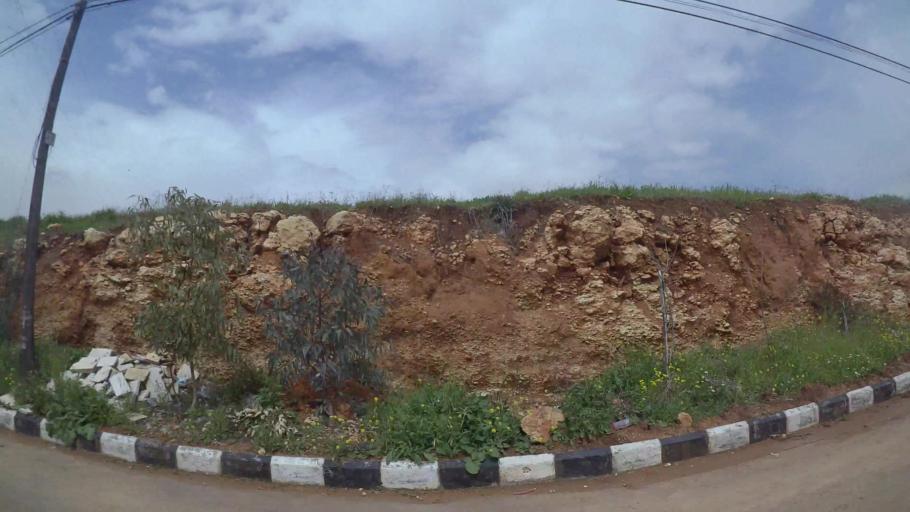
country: JO
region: Amman
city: Umm as Summaq
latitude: 31.9001
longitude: 35.8330
